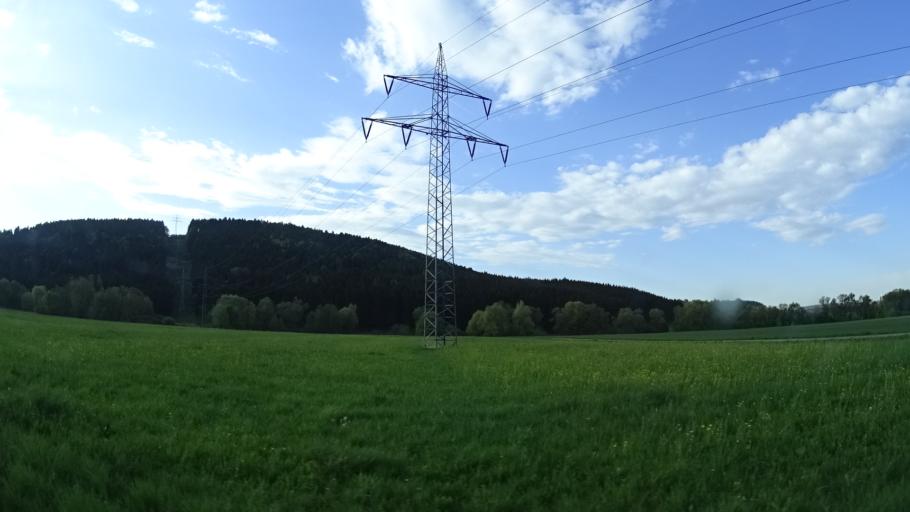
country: DE
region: Baden-Wuerttemberg
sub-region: Freiburg Region
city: Dietingen
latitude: 48.2517
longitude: 8.6689
